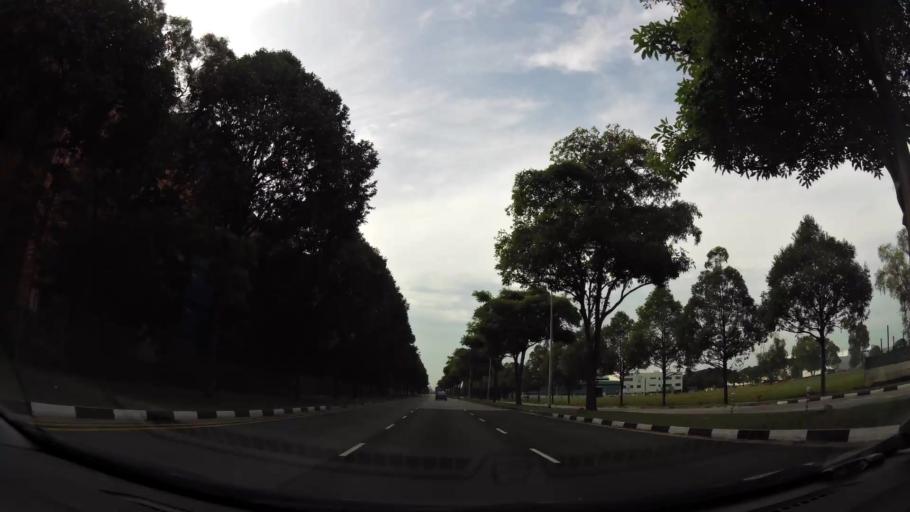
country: MY
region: Johor
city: Johor Bahru
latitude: 1.2924
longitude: 103.6315
